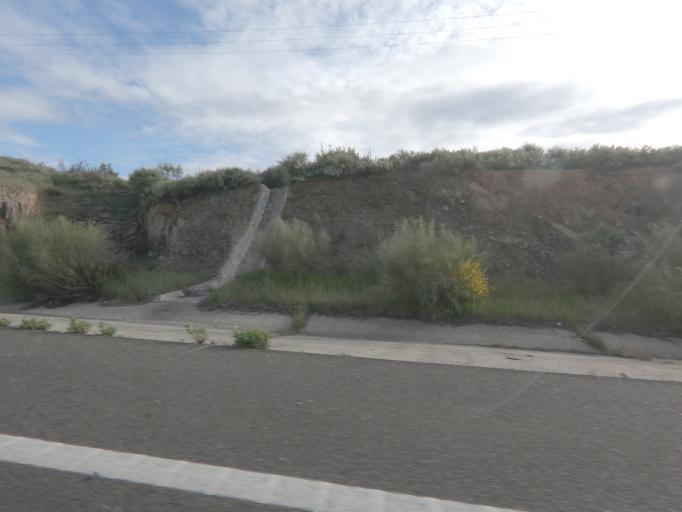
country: ES
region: Extremadura
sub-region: Provincia de Caceres
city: Casas de Don Gomez
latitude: 40.0240
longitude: -6.6013
